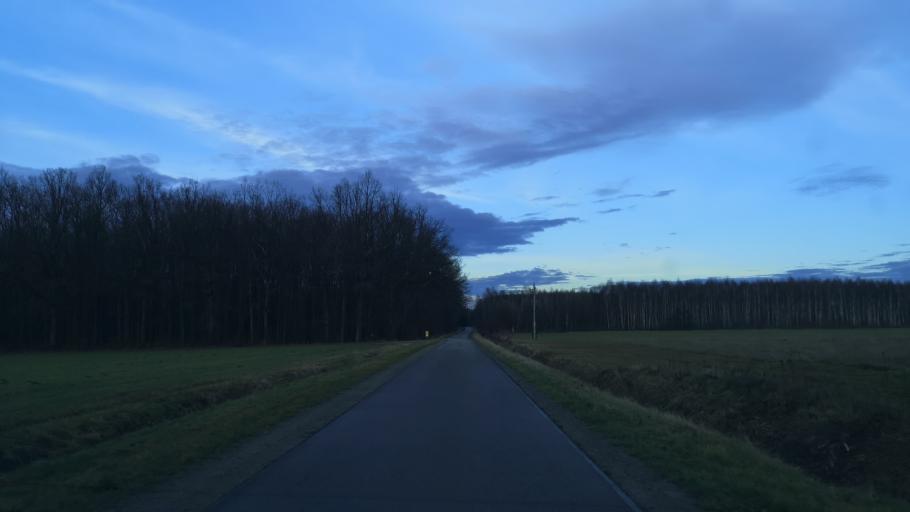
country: PL
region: Subcarpathian Voivodeship
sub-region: Powiat przeworski
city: Adamowka
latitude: 50.2574
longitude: 22.6431
